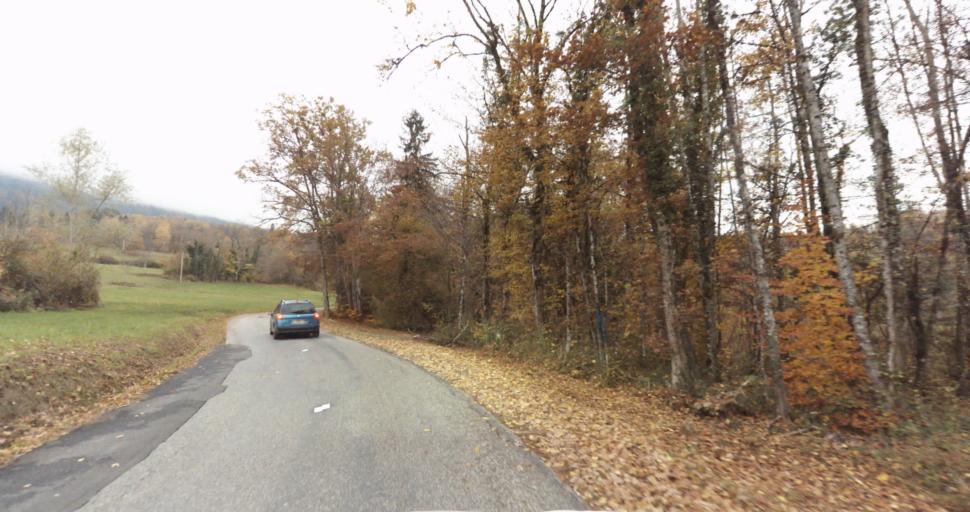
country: FR
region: Rhone-Alpes
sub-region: Departement de la Haute-Savoie
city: Saint-Jorioz
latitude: 45.8205
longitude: 6.1692
